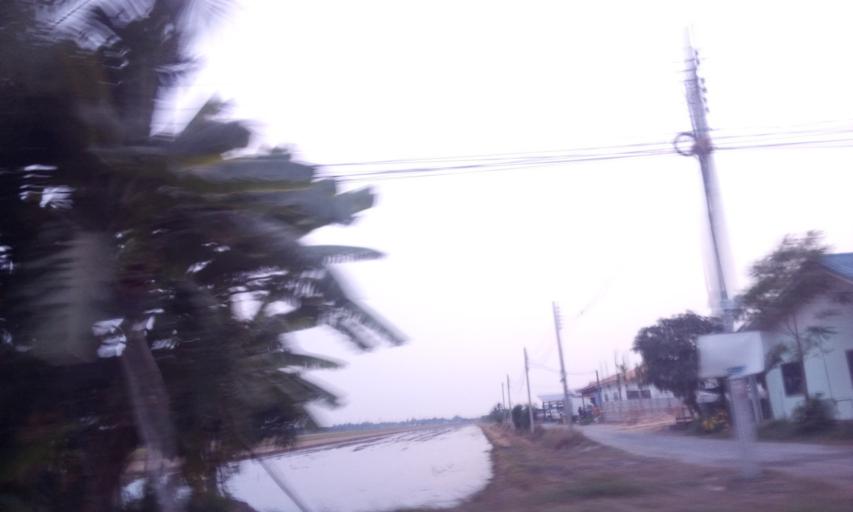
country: TH
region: Bangkok
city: Nong Chok
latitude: 13.8203
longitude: 100.9283
